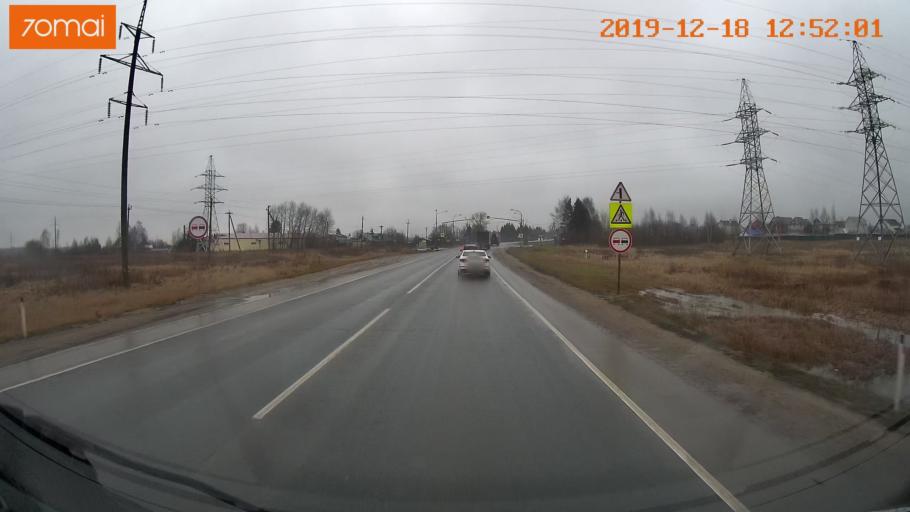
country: RU
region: Moskovskaya
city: Klin
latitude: 56.3087
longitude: 36.6860
